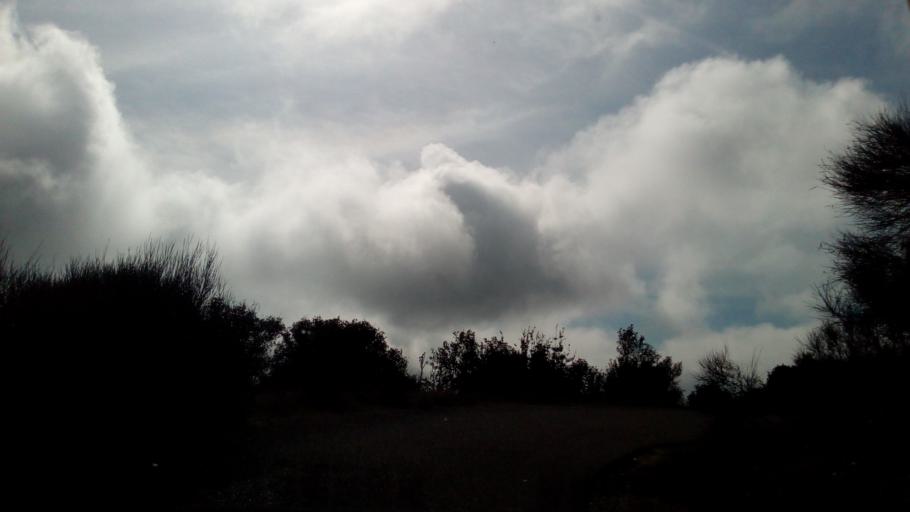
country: GR
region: West Greece
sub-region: Nomos Achaias
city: Kamarai
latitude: 38.4563
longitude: 21.9824
